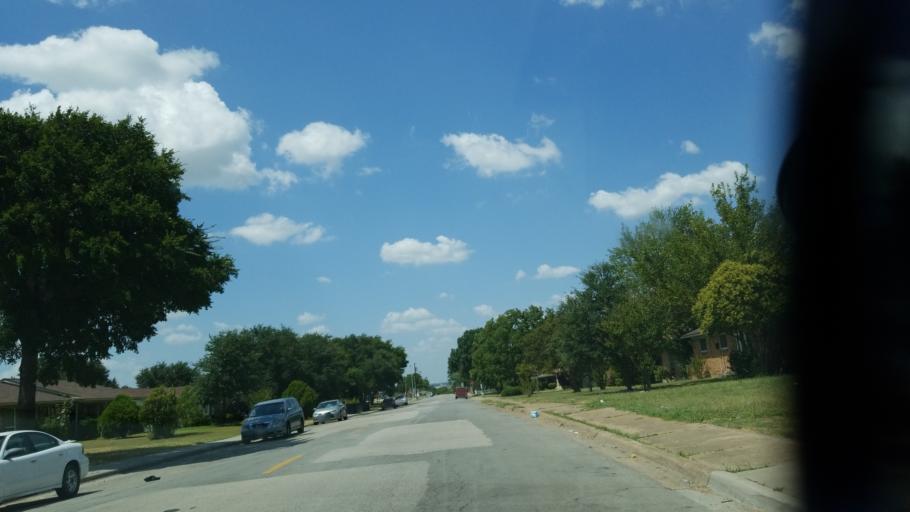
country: US
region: Texas
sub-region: Dallas County
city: Cockrell Hill
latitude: 32.7364
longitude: -96.9220
